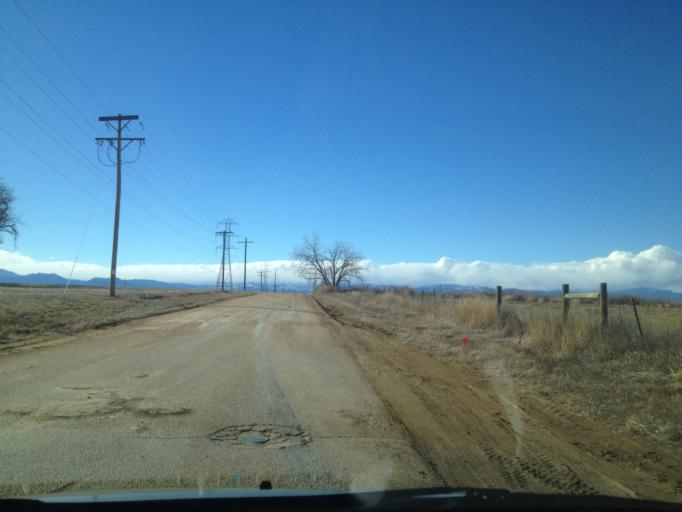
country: US
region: Colorado
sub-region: Weld County
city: Dacono
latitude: 40.0586
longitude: -104.9613
